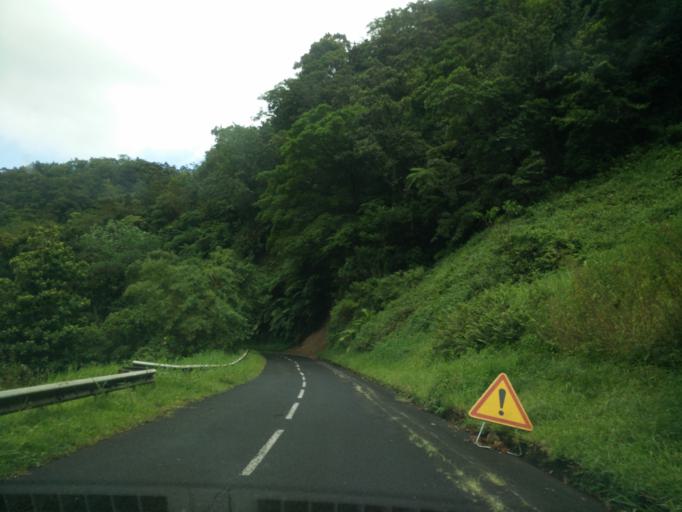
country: MQ
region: Martinique
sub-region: Martinique
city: Le Morne-Rouge
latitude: 14.7263
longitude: -61.1097
